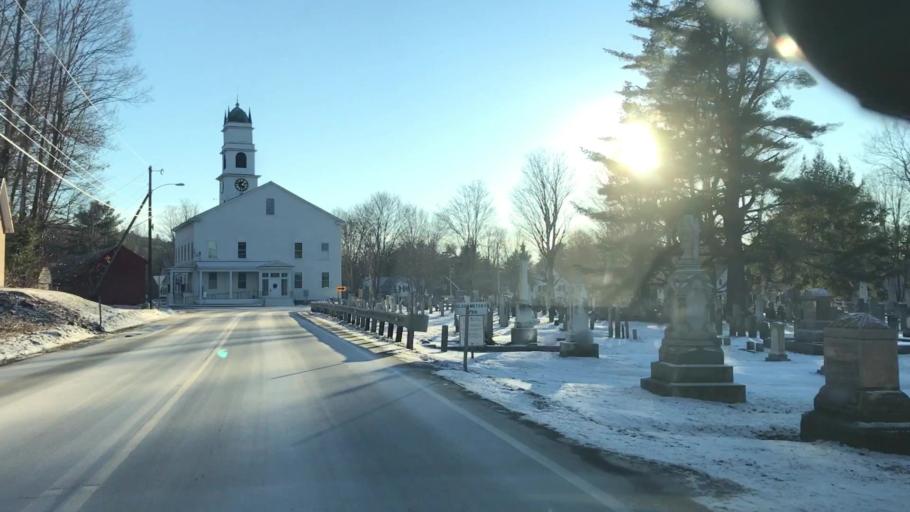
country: US
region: New Hampshire
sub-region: Grafton County
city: Lyme
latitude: 43.8116
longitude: -72.1547
